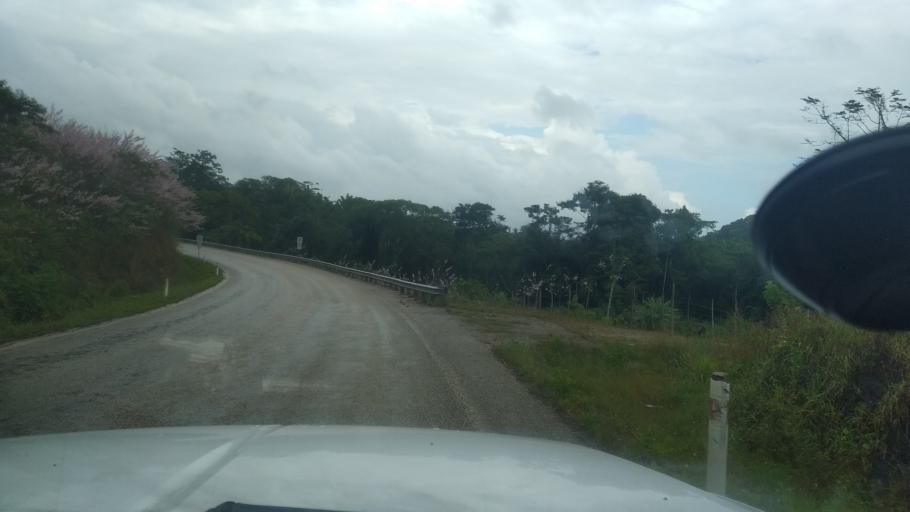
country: GT
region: Peten
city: San Luis
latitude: 16.1867
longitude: -89.1911
